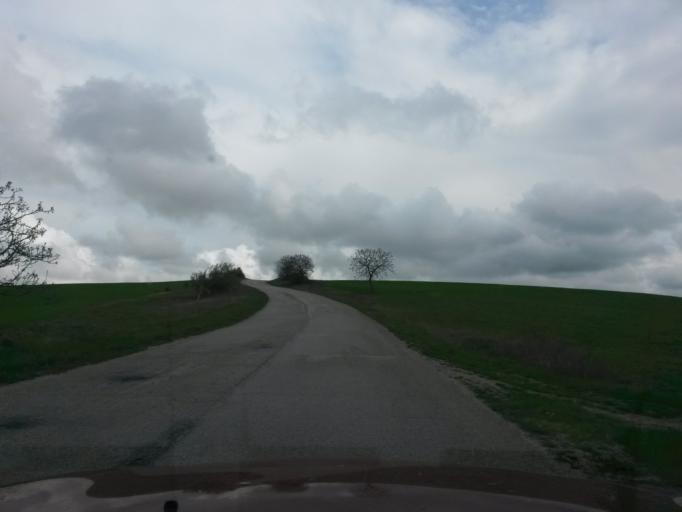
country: SK
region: Kosicky
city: Roznava
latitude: 48.5604
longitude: 20.4948
